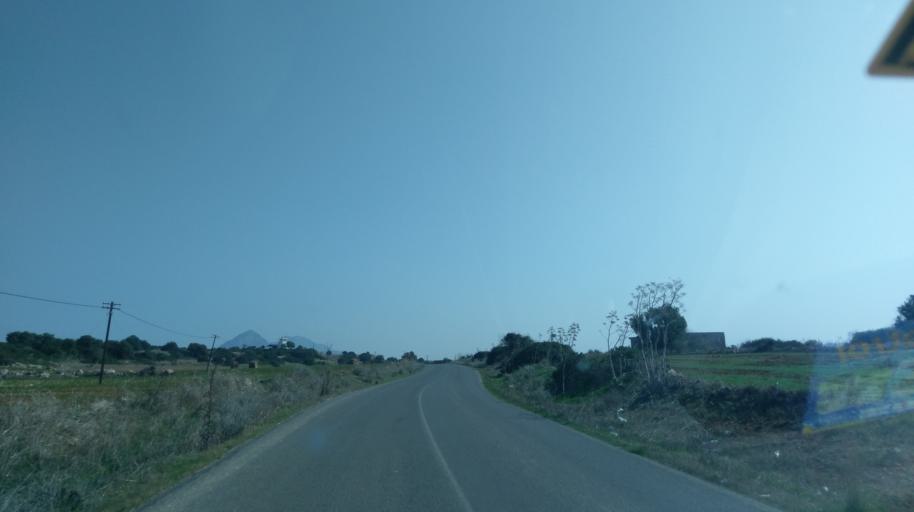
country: CY
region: Lefkosia
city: Morfou
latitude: 35.3406
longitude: 33.0204
